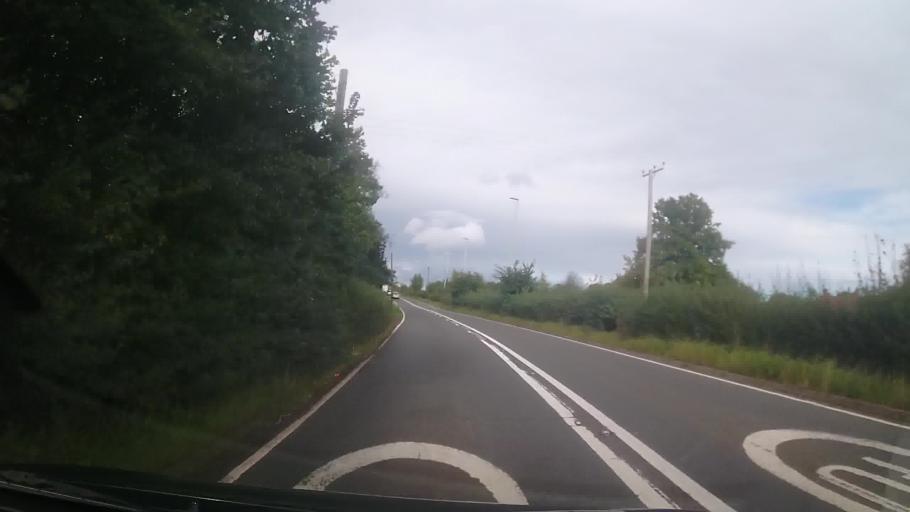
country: GB
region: England
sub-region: Shropshire
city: Alveley
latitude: 52.4559
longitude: -2.3420
